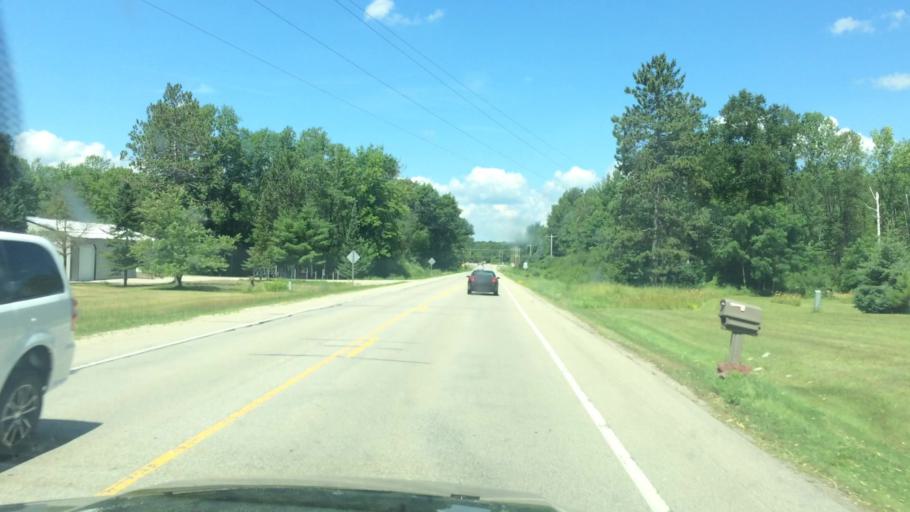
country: US
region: Wisconsin
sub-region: Marinette County
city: Peshtigo
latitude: 45.1018
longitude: -87.7457
